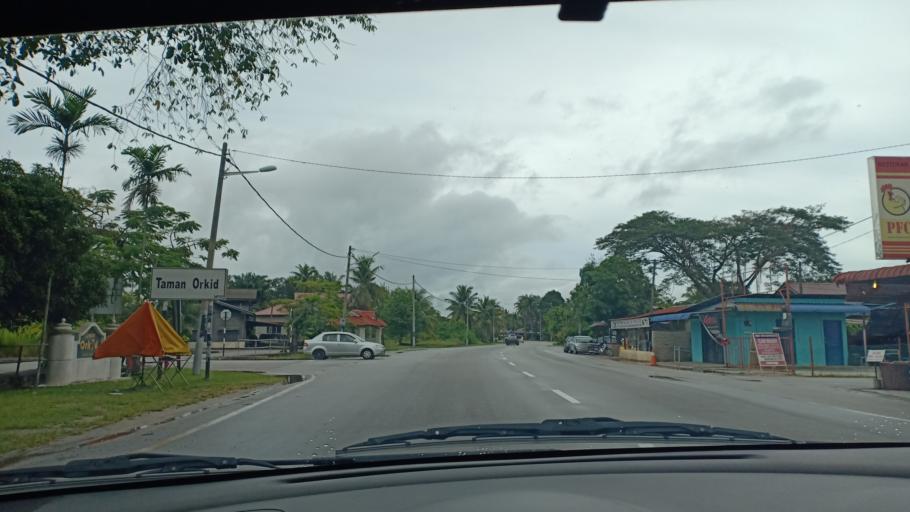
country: MY
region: Penang
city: Kepala Batas
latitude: 5.4957
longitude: 100.4461
